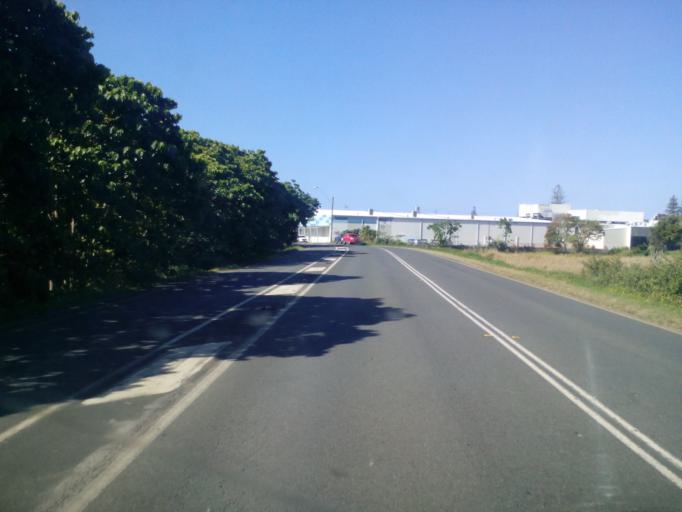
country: AU
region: New South Wales
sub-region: Tweed
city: Kingscliff
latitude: -28.2567
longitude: 153.5728
